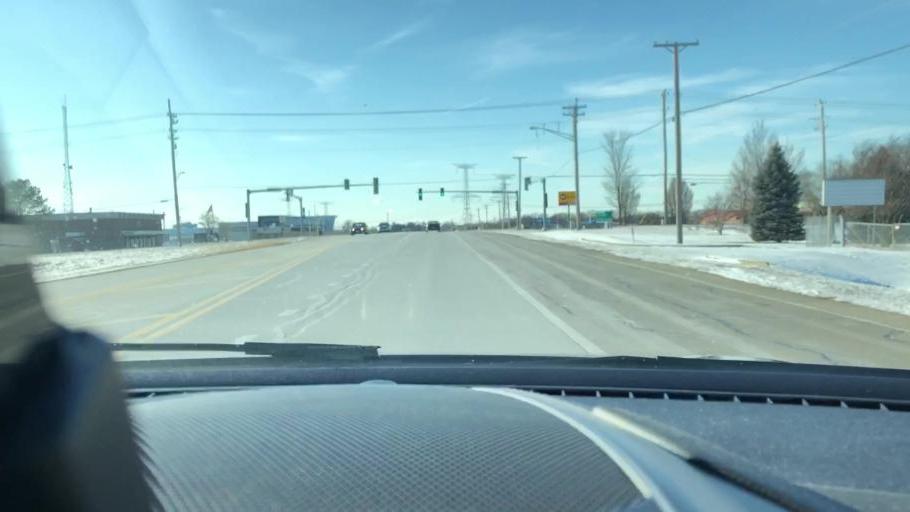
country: US
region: Illinois
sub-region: Will County
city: Ingalls Park
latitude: 41.4822
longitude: -88.0212
